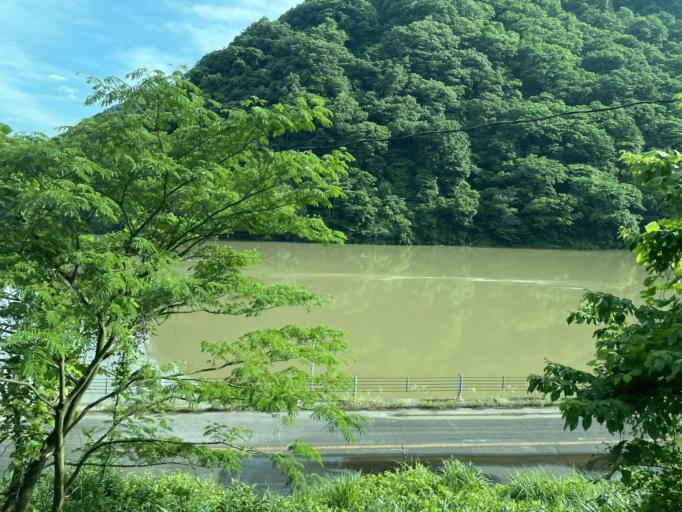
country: JP
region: Niigata
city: Suibara
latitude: 37.6976
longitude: 139.4153
